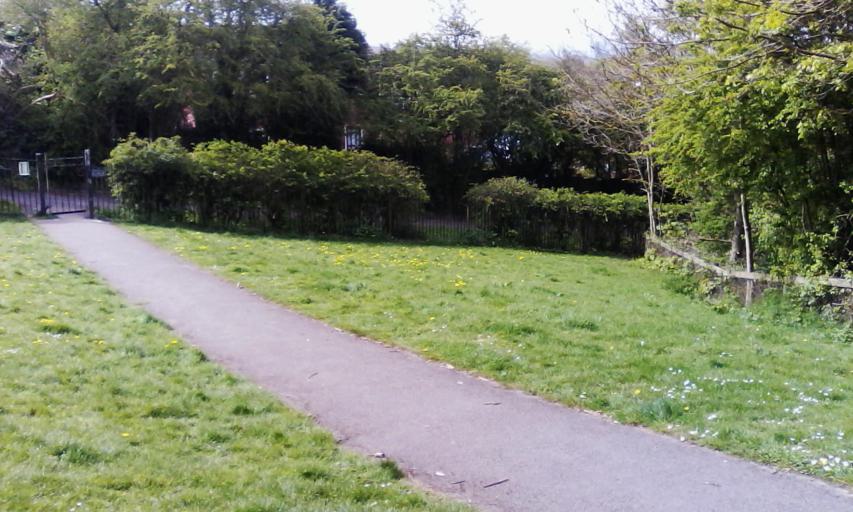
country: GB
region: England
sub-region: Nottinghamshire
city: Arnold
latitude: 52.9727
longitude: -1.1219
